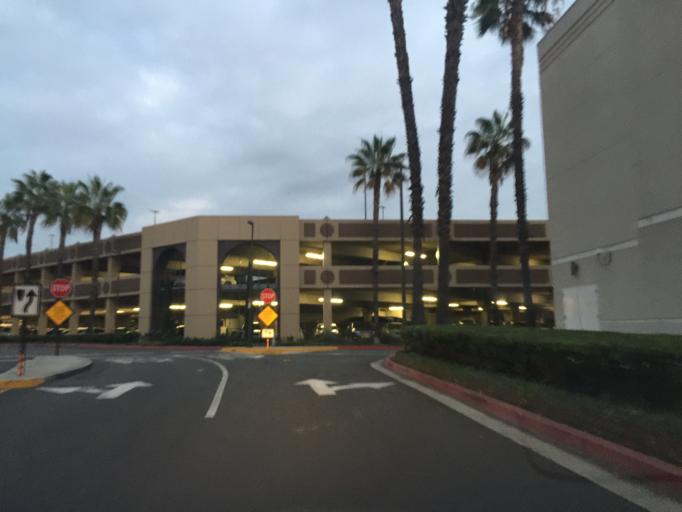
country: US
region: California
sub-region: Orange County
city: Brea
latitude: 33.9171
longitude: -117.8866
